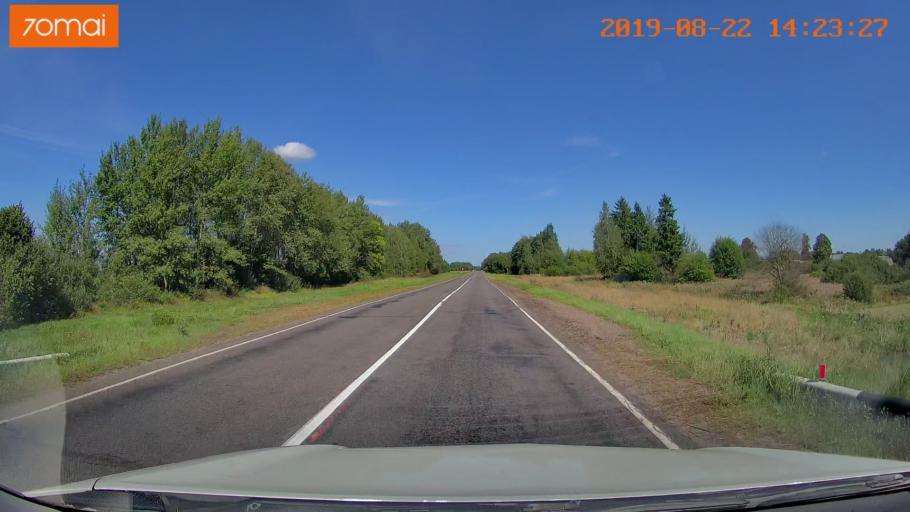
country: BY
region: Mogilev
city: Asipovichy
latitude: 53.2891
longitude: 28.5837
